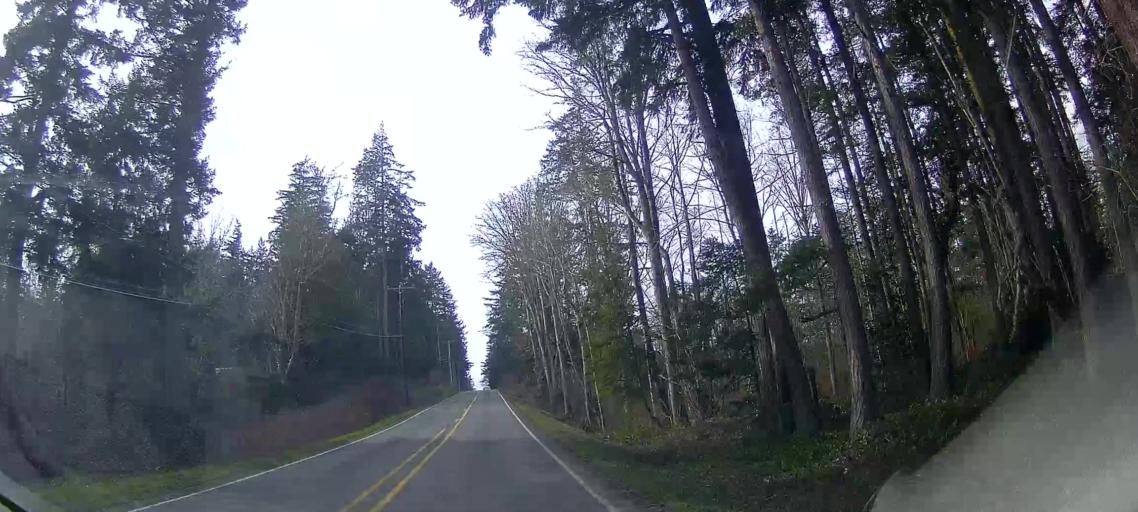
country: US
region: Washington
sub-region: Island County
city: Camano
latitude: 48.1384
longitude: -122.4855
